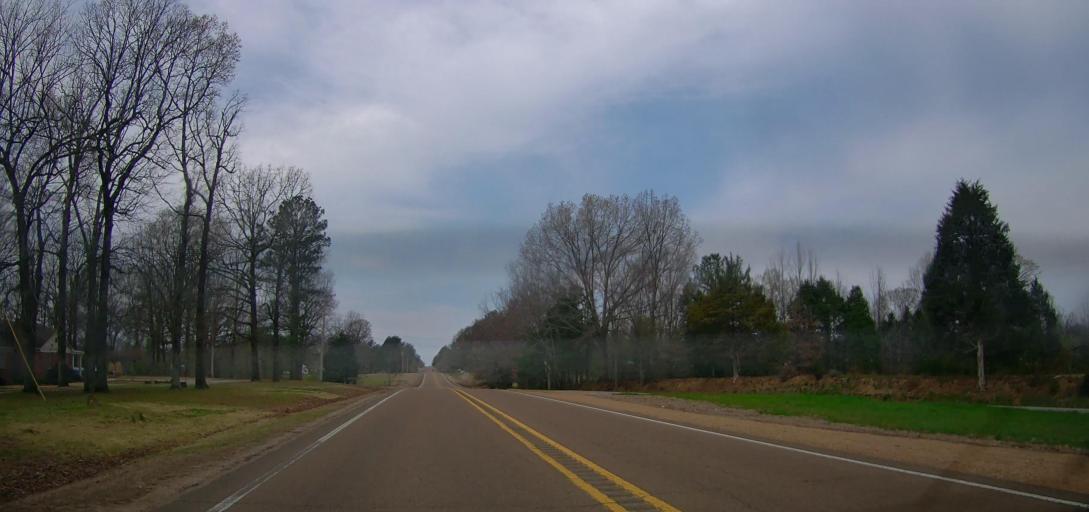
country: US
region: Mississippi
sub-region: Marshall County
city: Byhalia
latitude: 34.8358
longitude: -89.5875
